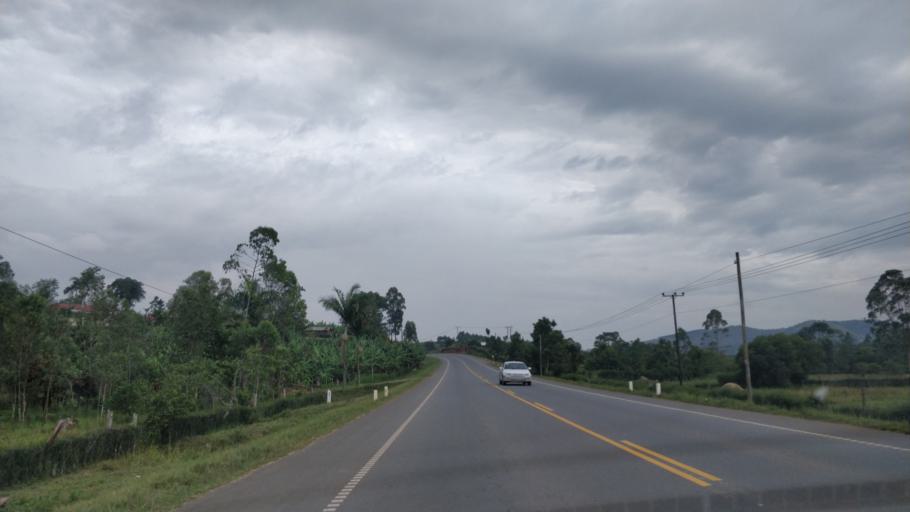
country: UG
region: Western Region
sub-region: Sheema District
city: Kibingo
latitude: -0.6560
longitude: 30.4784
